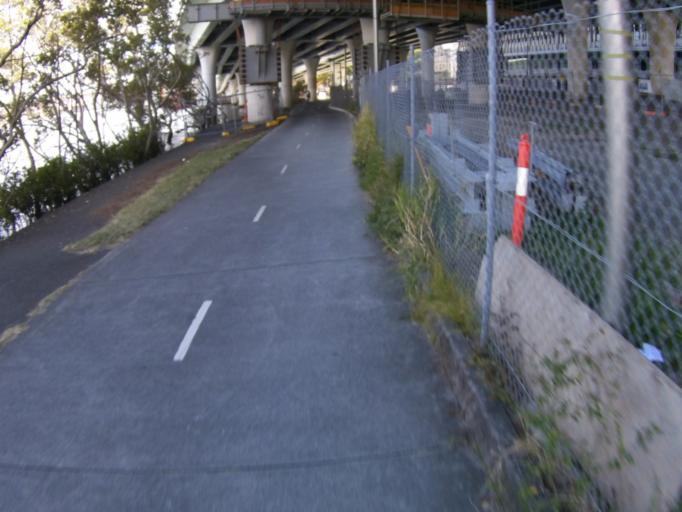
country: AU
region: Queensland
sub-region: Brisbane
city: South Brisbane
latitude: -27.4750
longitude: 153.0246
